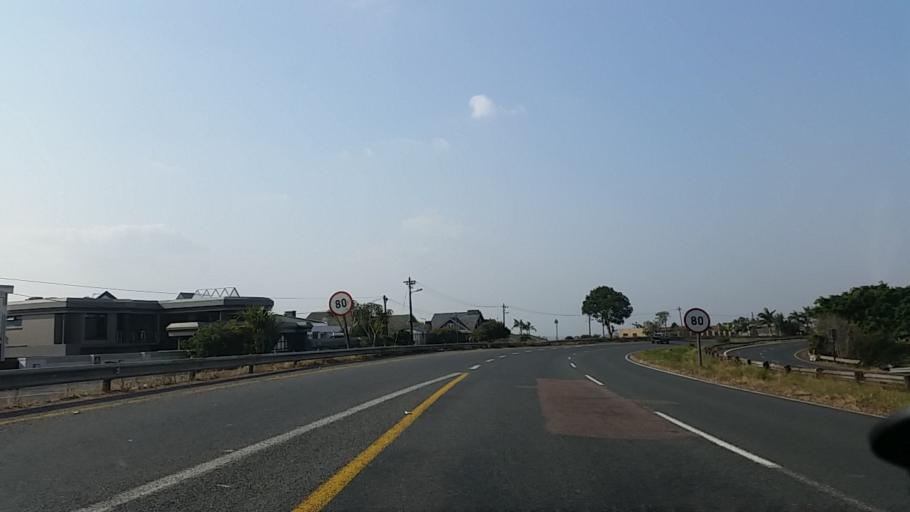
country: ZA
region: KwaZulu-Natal
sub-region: eThekwini Metropolitan Municipality
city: Berea
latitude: -29.8302
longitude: 30.9438
